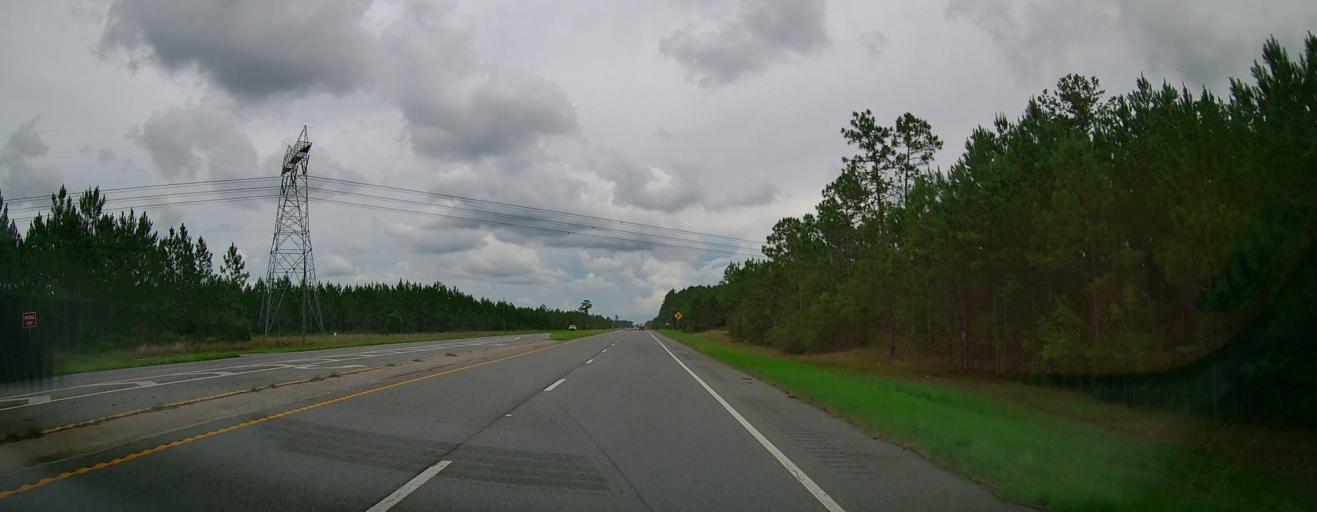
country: US
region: Georgia
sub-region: Wayne County
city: Jesup
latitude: 31.6793
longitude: -82.0867
